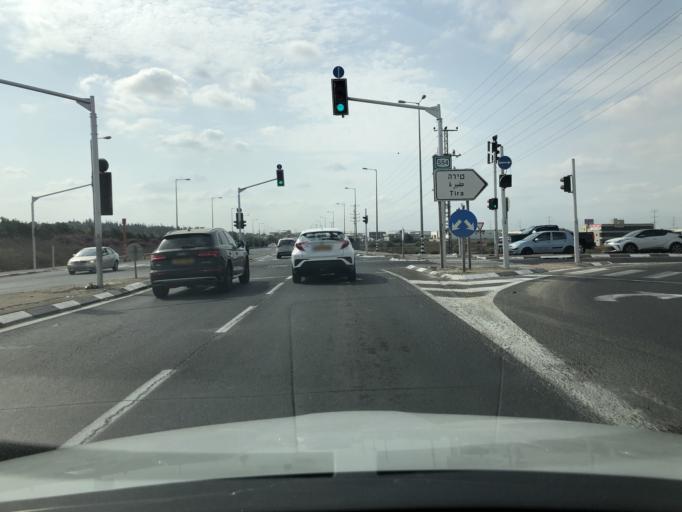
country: IL
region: Central District
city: Tirah
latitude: 32.2322
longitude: 34.9843
